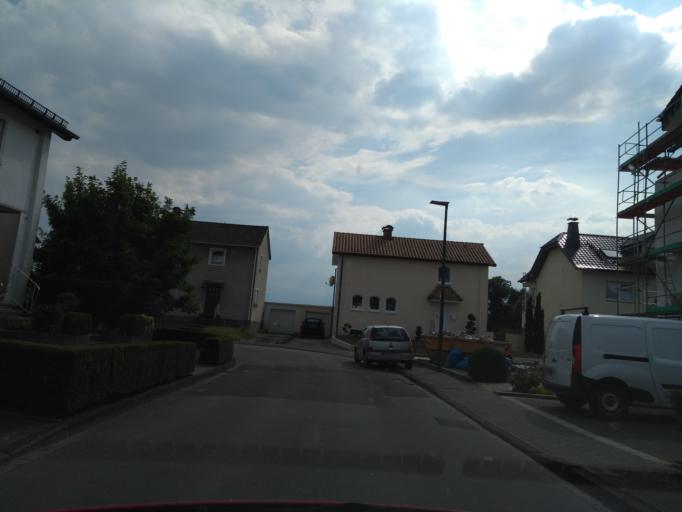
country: DE
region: North Rhine-Westphalia
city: Bad Lippspringe
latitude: 51.7653
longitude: 8.7930
